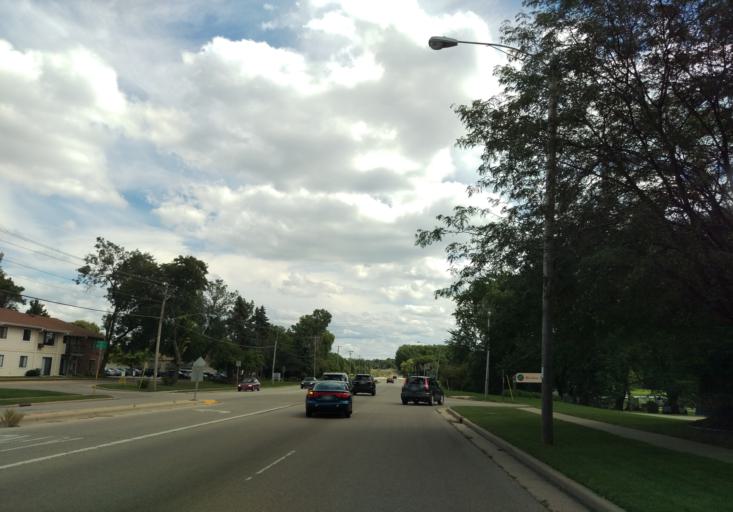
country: US
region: Wisconsin
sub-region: Dane County
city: Middleton
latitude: 43.1118
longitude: -89.4698
